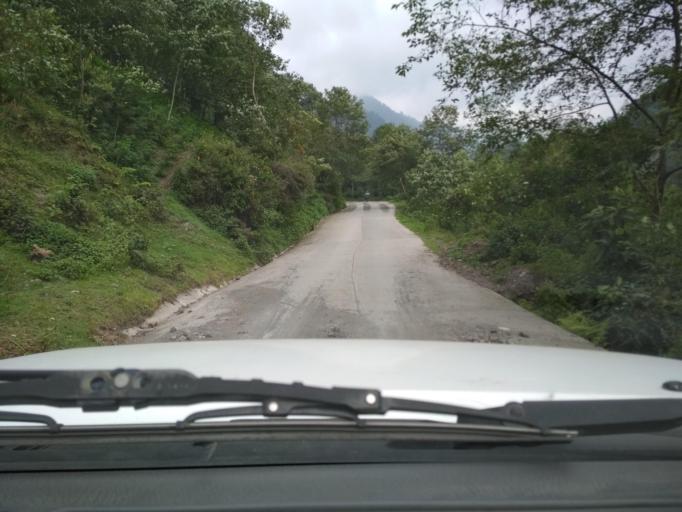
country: MX
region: Veracruz
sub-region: La Perla
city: Metlac Hernandez (Metlac Primero)
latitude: 18.9804
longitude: -97.1376
